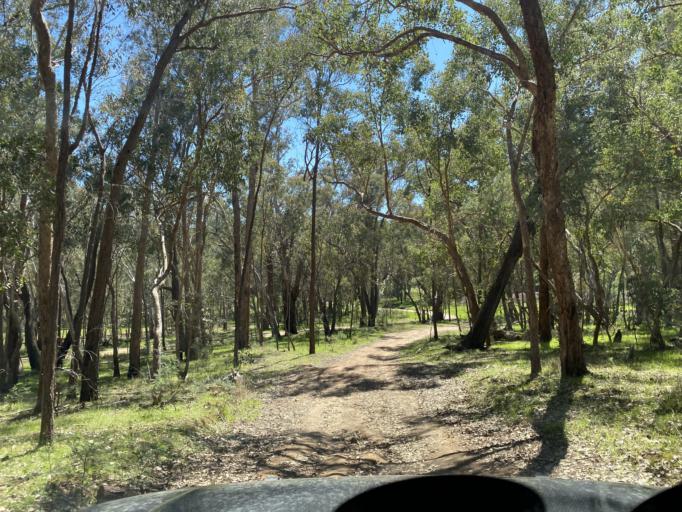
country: AU
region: Victoria
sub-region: Benalla
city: Benalla
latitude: -36.6949
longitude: 146.1480
